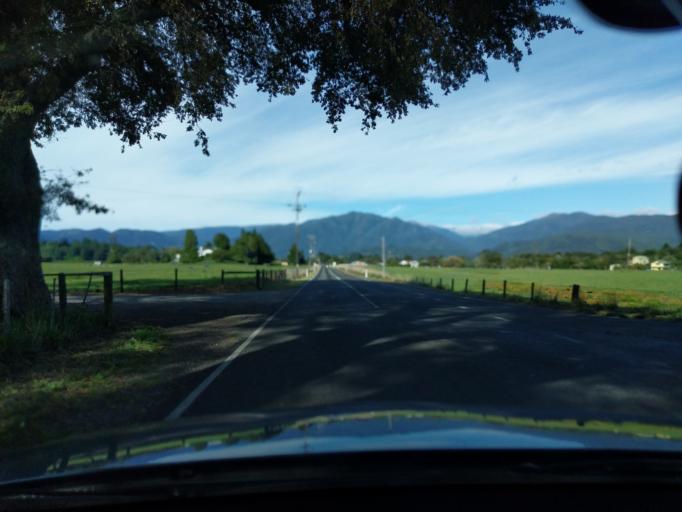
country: NZ
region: Tasman
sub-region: Tasman District
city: Takaka
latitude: -40.8517
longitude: 172.8298
